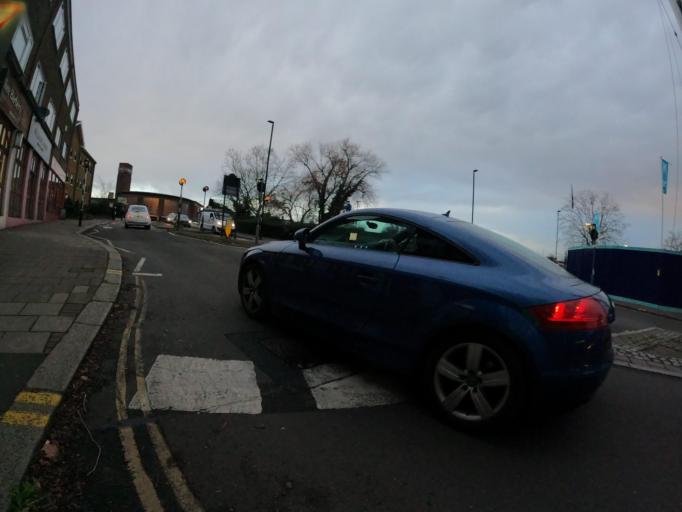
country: GB
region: England
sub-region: Greater London
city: Acton
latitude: 51.4936
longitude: -0.2676
